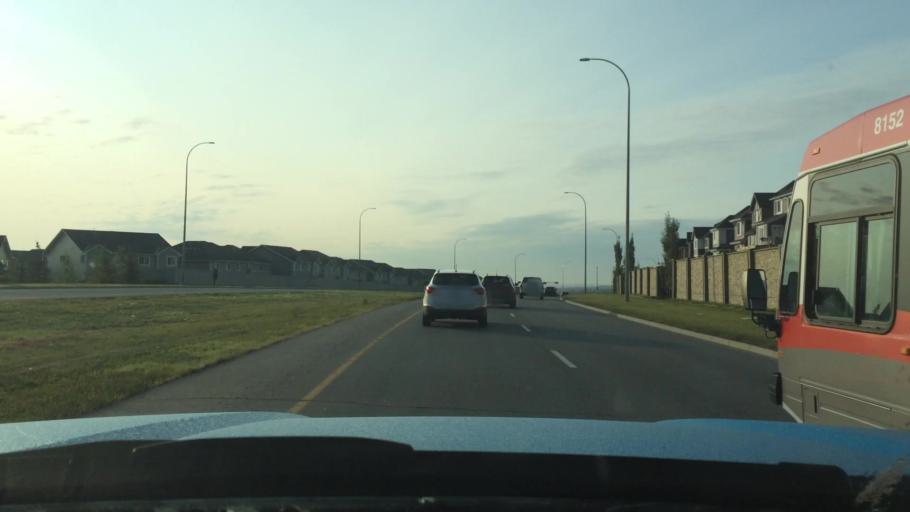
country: CA
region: Alberta
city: Calgary
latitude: 51.1650
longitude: -114.1473
